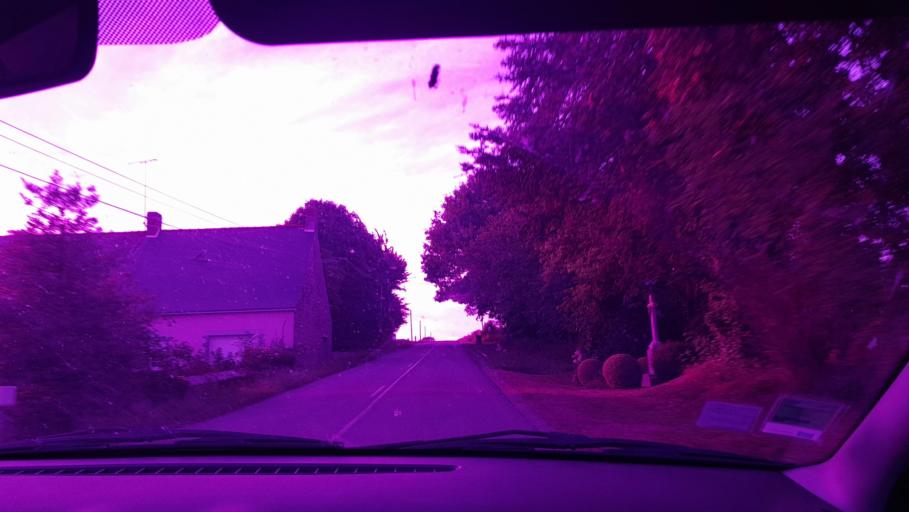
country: FR
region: Brittany
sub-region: Departement d'Ille-et-Vilaine
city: Le Pertre
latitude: 47.9808
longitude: -1.0414
